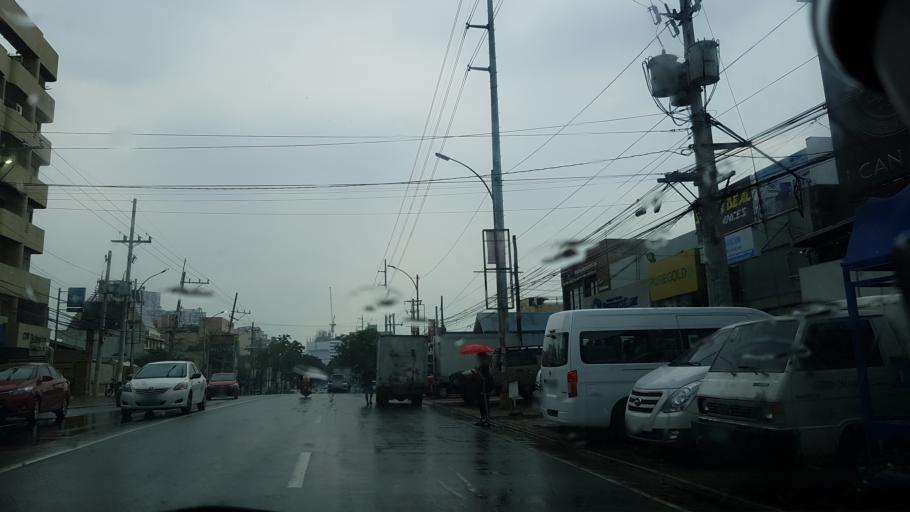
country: PH
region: Calabarzon
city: Del Monte
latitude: 14.6446
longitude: 121.0275
